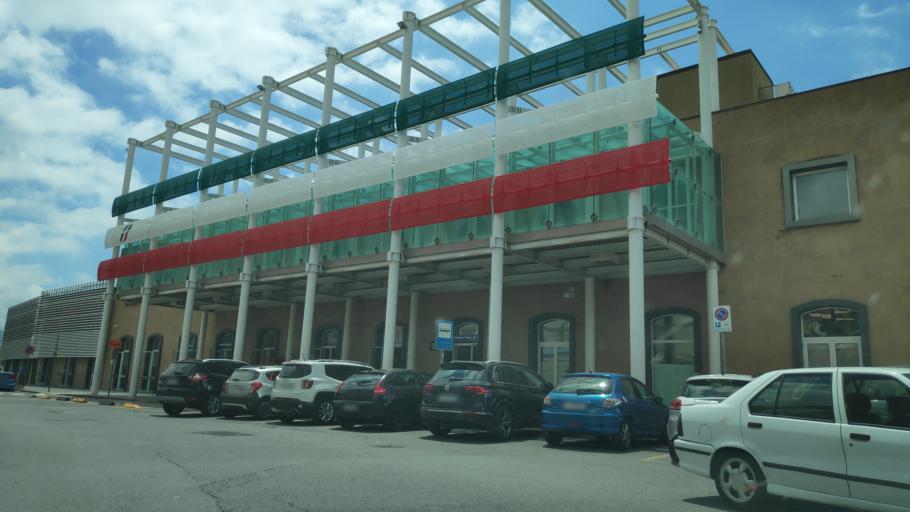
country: IT
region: Calabria
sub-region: Provincia di Cosenza
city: Paola
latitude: 39.3598
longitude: 16.0333
